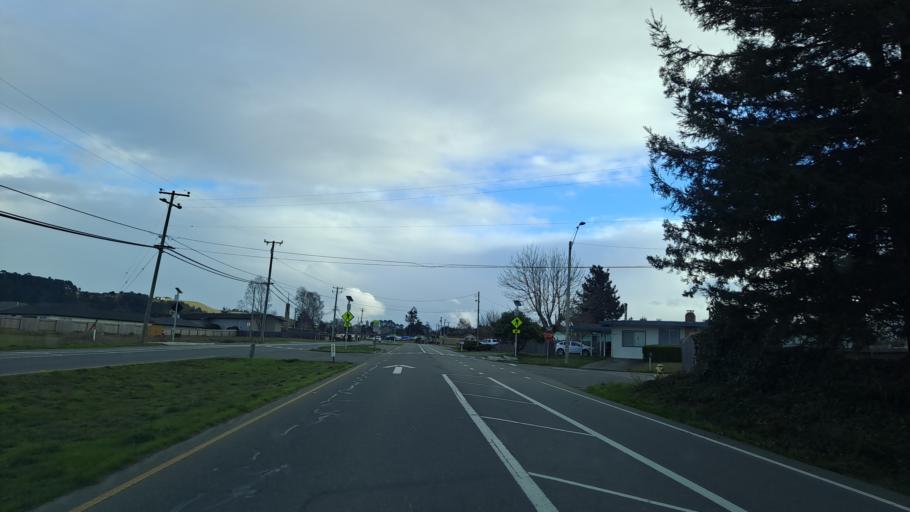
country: US
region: California
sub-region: Humboldt County
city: Fortuna
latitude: 40.5732
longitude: -124.1426
